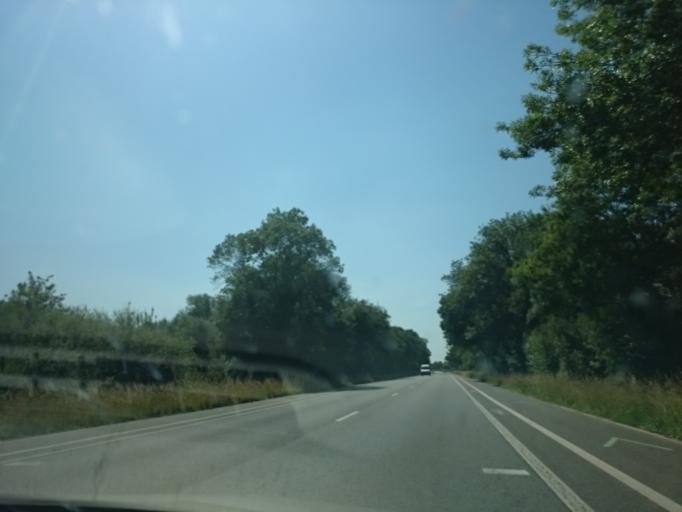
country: FR
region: Pays de la Loire
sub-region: Departement de la Loire-Atlantique
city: La Montagne
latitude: 47.2090
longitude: -1.6926
